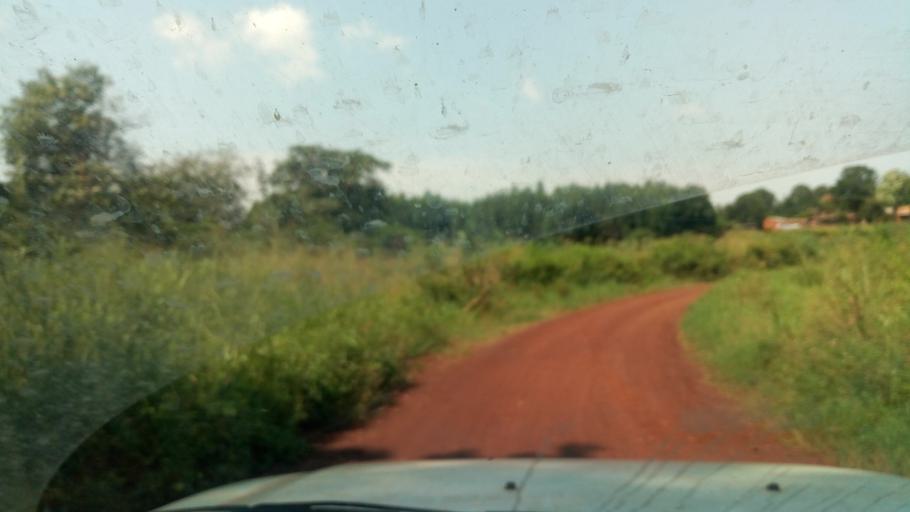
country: UG
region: Western Region
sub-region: Masindi District
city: Masindi
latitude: 1.6428
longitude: 31.8047
